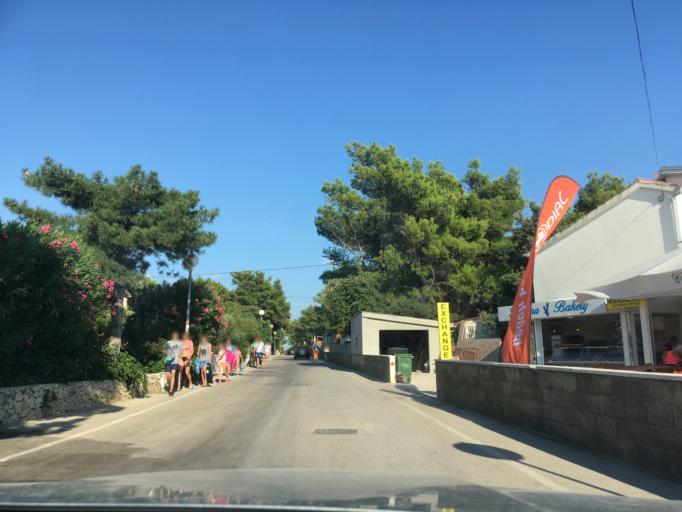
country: HR
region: Zadarska
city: Vir
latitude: 44.2981
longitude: 15.0964
